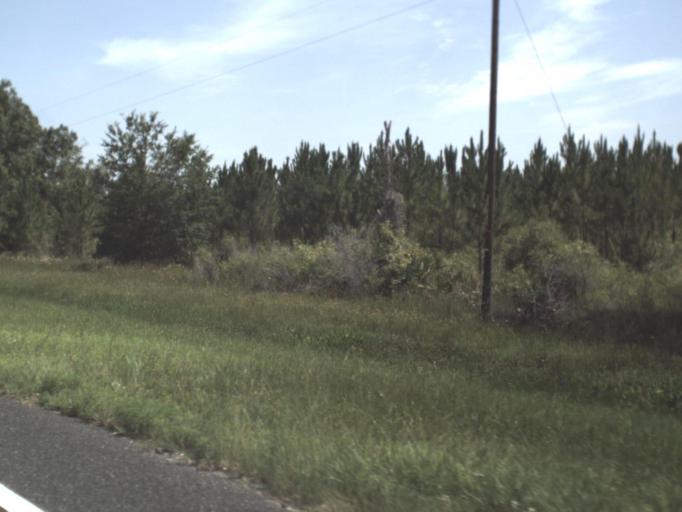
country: US
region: Florida
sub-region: Taylor County
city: Steinhatchee
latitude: 29.7371
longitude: -83.3166
